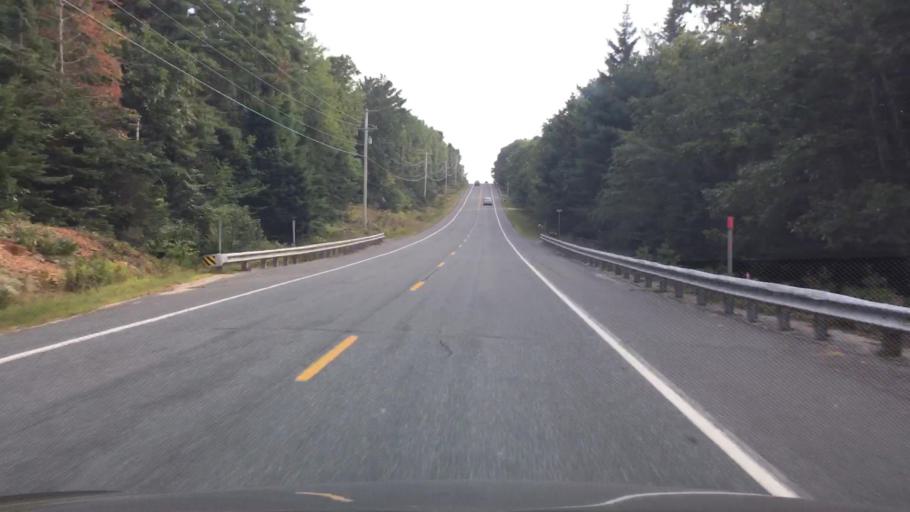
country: US
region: Maine
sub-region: Hancock County
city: Surry
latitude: 44.4830
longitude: -68.5159
